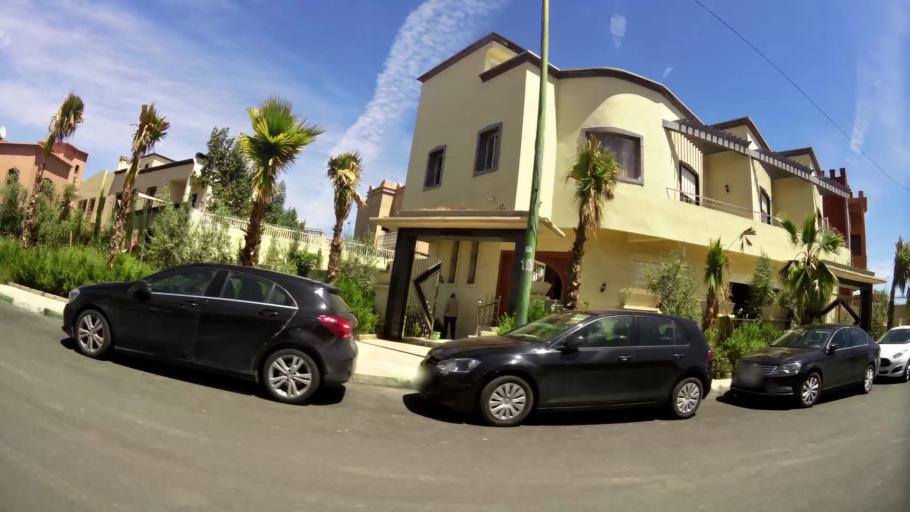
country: MA
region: Marrakech-Tensift-Al Haouz
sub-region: Marrakech
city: Marrakesh
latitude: 31.6416
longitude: -8.0462
